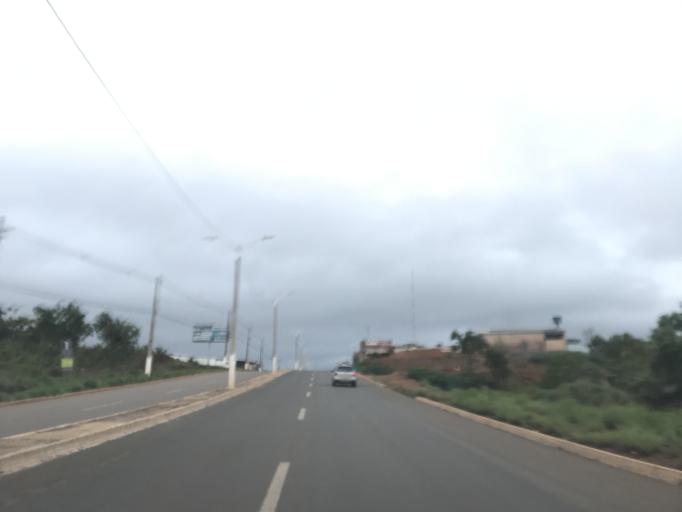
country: BR
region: Goias
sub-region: Luziania
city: Luziania
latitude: -16.2171
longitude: -47.9323
